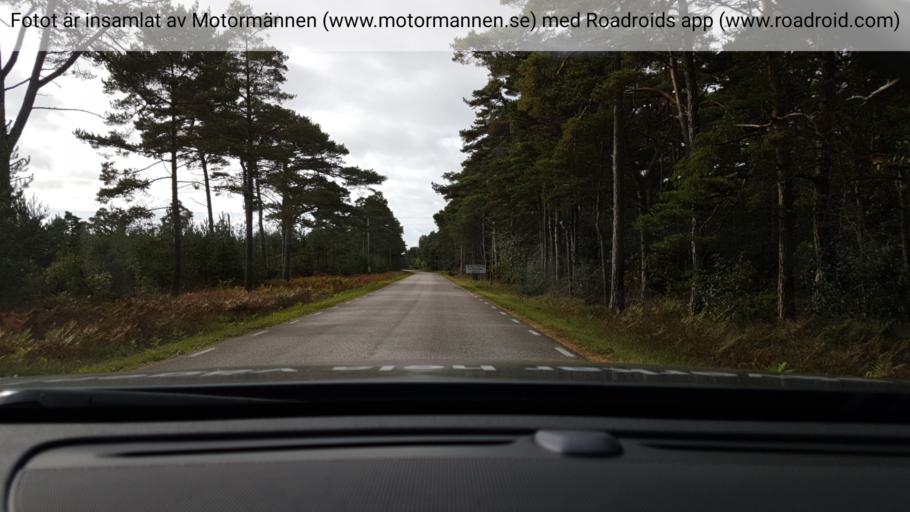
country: SE
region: Gotland
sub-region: Gotland
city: Hemse
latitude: 56.9571
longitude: 18.2160
